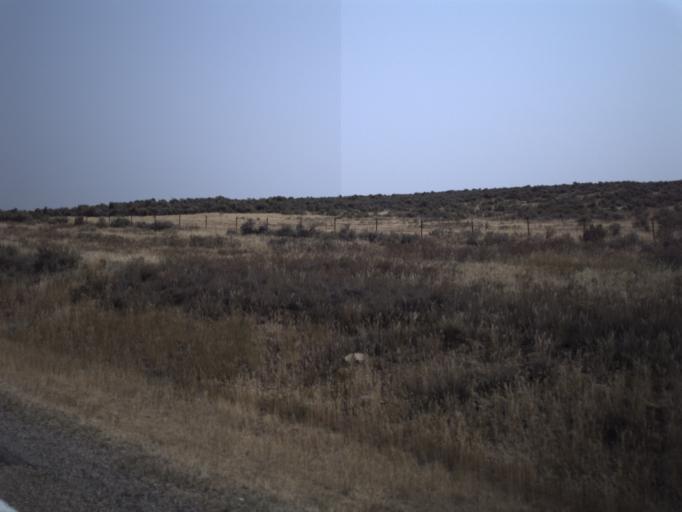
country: US
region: Utah
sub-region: Morgan County
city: Morgan
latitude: 40.9509
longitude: -111.5497
